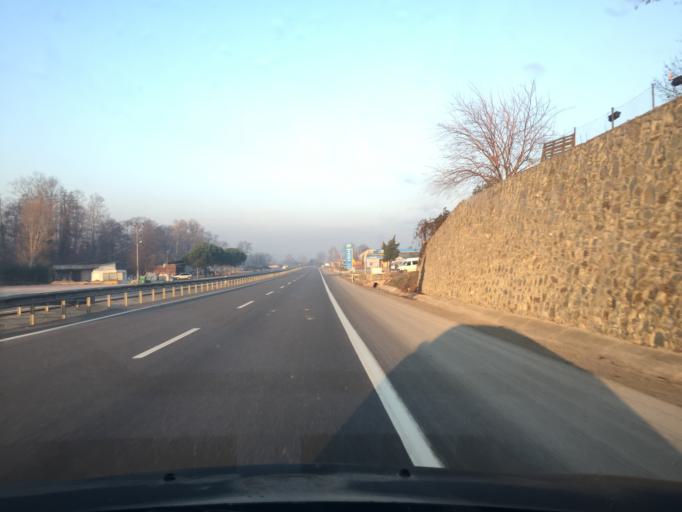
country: TR
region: Sakarya
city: Akyazi
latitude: 40.6309
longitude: 30.6381
